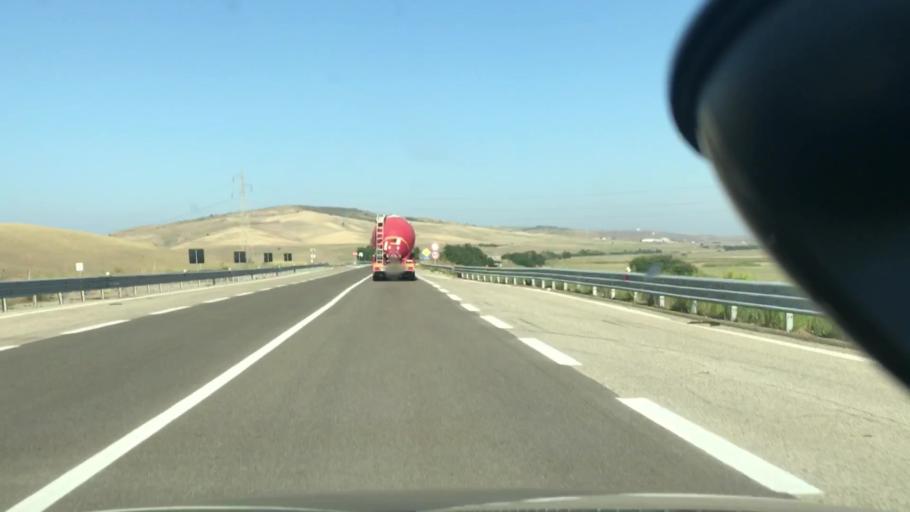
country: IT
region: Basilicate
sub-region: Provincia di Matera
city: Irsina
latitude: 40.7881
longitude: 16.2897
